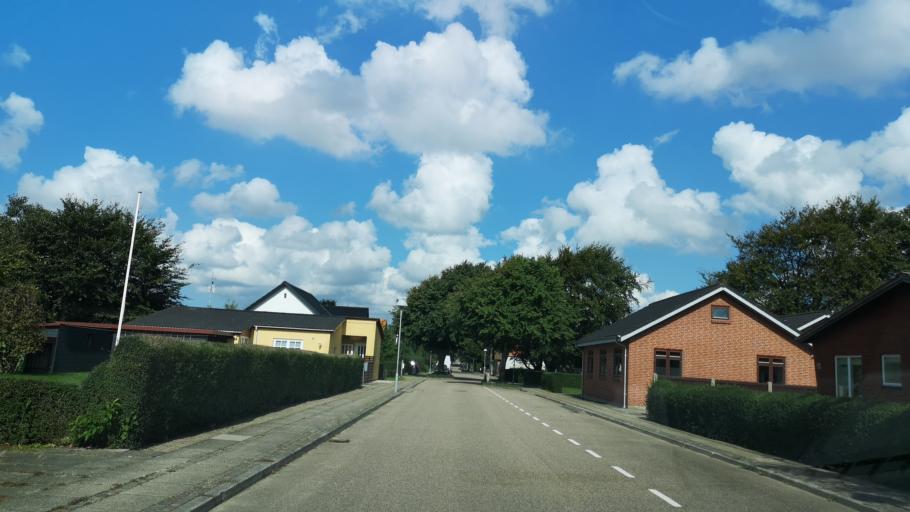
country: DK
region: Central Jutland
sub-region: Ringkobing-Skjern Kommune
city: Skjern
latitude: 55.9484
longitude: 8.4881
